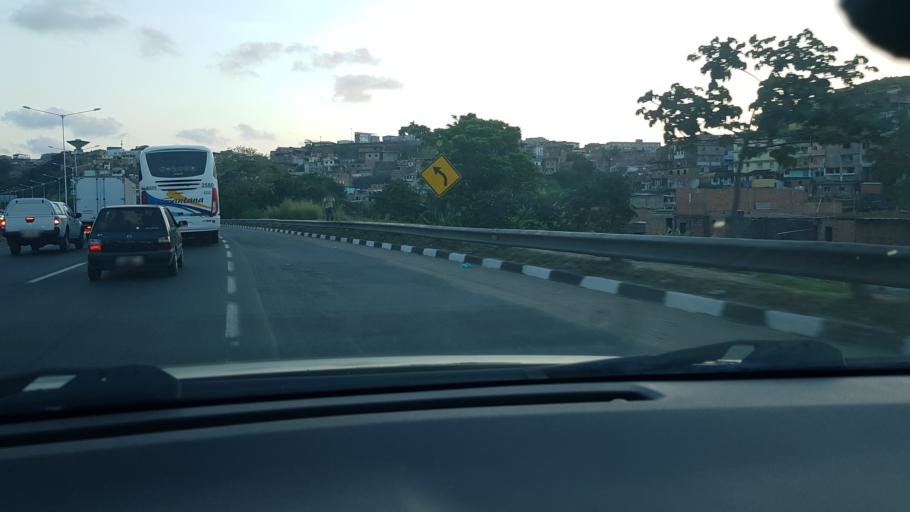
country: BR
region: Bahia
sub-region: Salvador
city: Salvador
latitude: -12.9303
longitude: -38.4703
